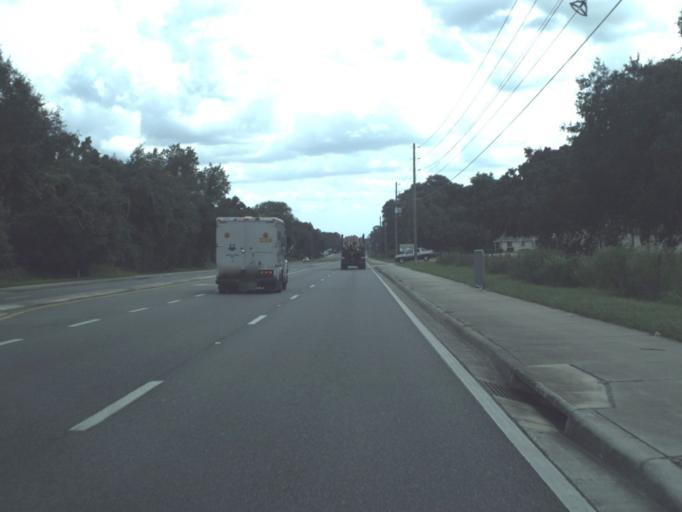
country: US
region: Florida
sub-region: Citrus County
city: Inverness Highlands South
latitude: 28.8026
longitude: -82.3101
